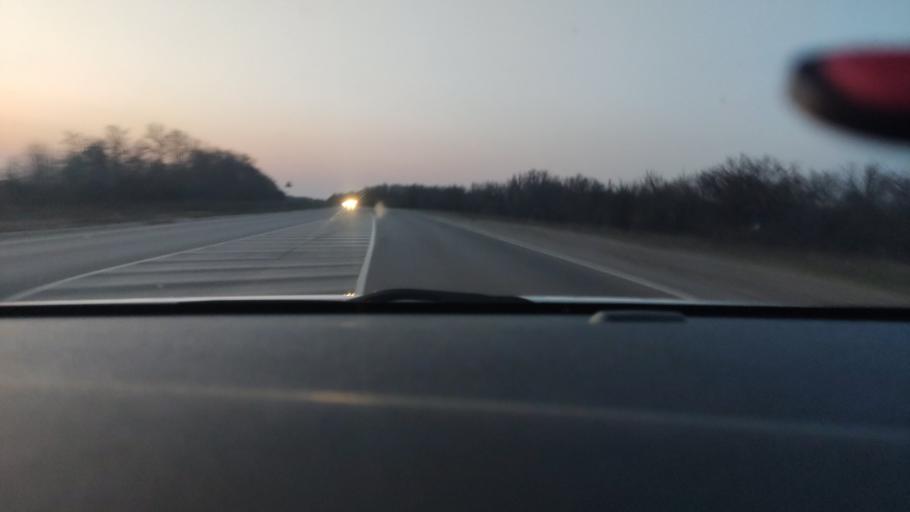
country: RU
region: Voronezj
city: Kolodeznyy
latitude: 51.3740
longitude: 39.0216
